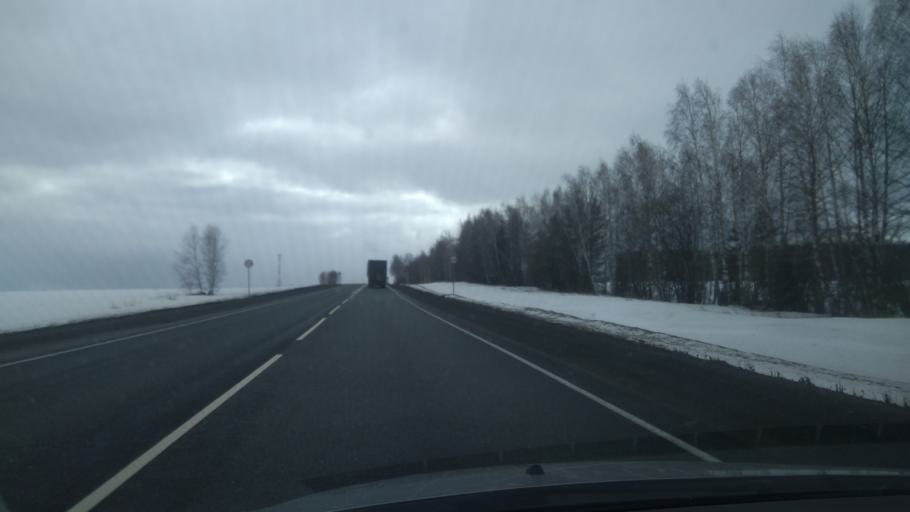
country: RU
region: Perm
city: Suksun
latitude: 56.9620
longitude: 57.5219
